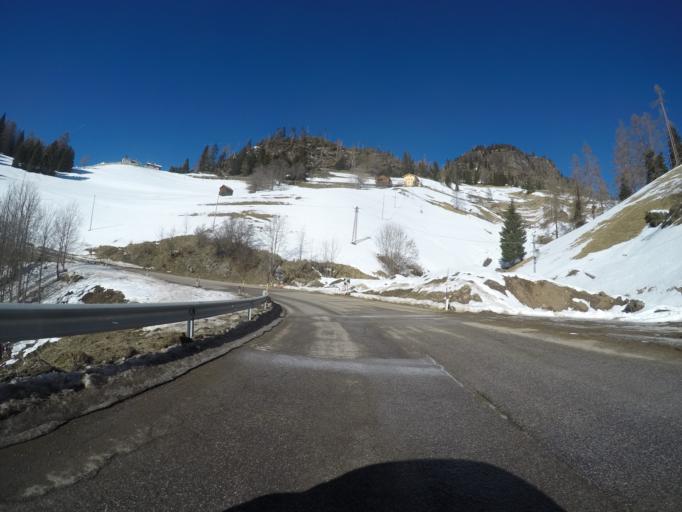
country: IT
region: Veneto
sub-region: Provincia di Belluno
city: Colle Santa Lucia
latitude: 46.4466
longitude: 12.0071
